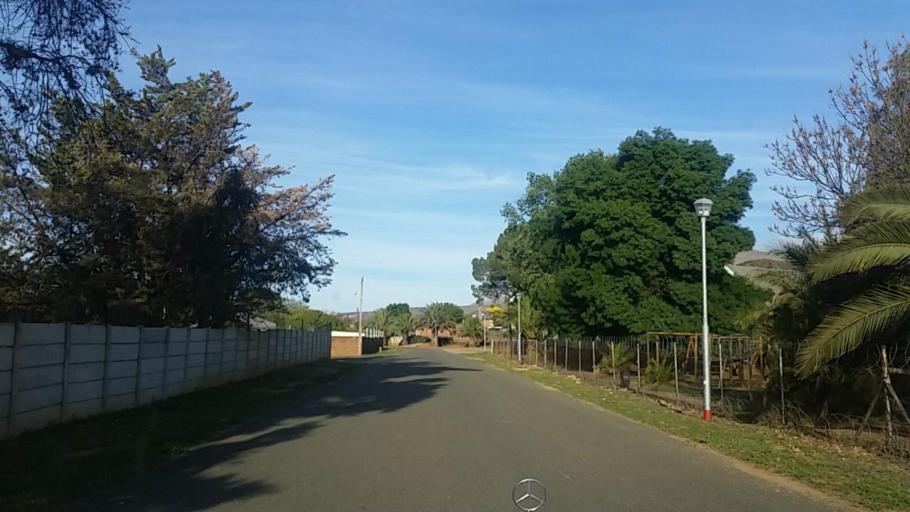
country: ZA
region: Western Cape
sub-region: Eden District Municipality
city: Knysna
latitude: -33.6559
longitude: 23.1237
